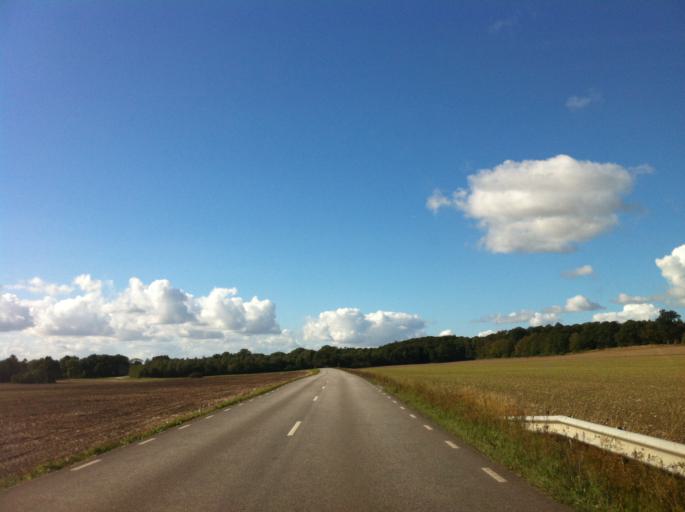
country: SE
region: Skane
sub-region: Sjobo Kommun
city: Blentarp
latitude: 55.6993
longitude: 13.5954
